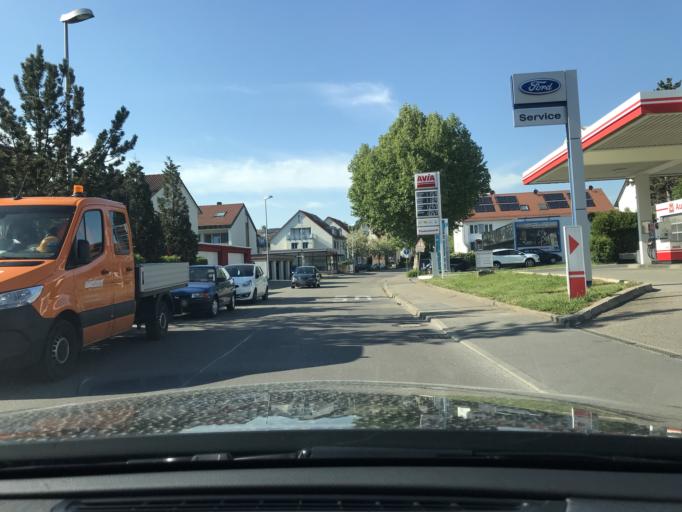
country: DE
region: Baden-Wuerttemberg
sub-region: Regierungsbezirk Stuttgart
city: Weinstadt-Endersbach
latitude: 48.8185
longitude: 9.3481
